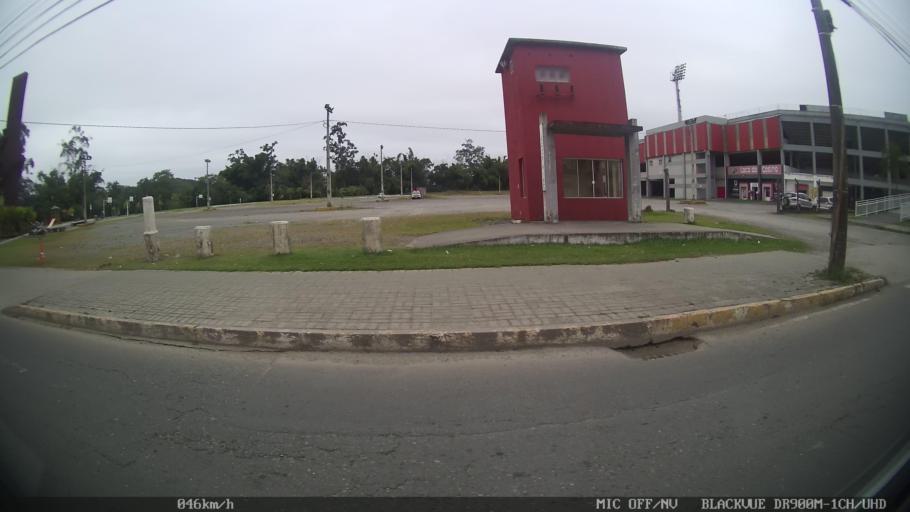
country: BR
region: Santa Catarina
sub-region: Joinville
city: Joinville
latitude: -26.3157
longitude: -48.8322
